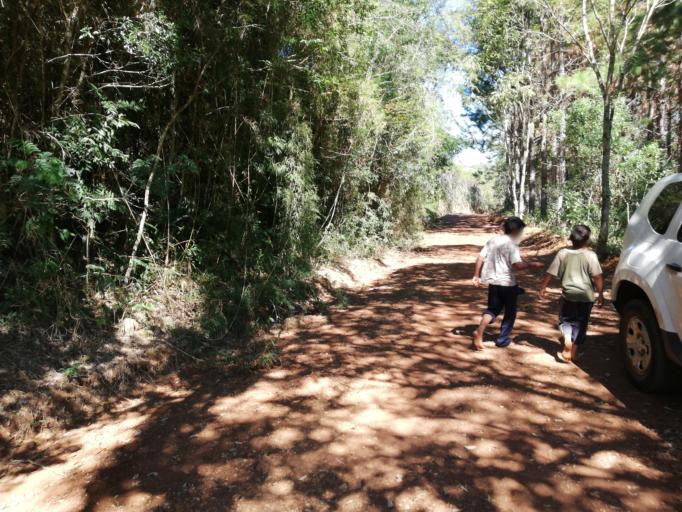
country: AR
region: Misiones
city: El Soberbio
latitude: -27.0633
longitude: -54.3775
